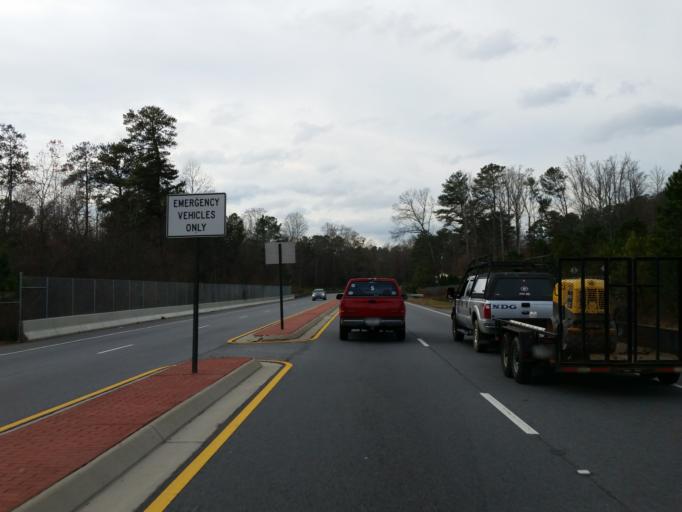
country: US
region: Georgia
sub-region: Cobb County
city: Fair Oaks
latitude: 33.8985
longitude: -84.5959
